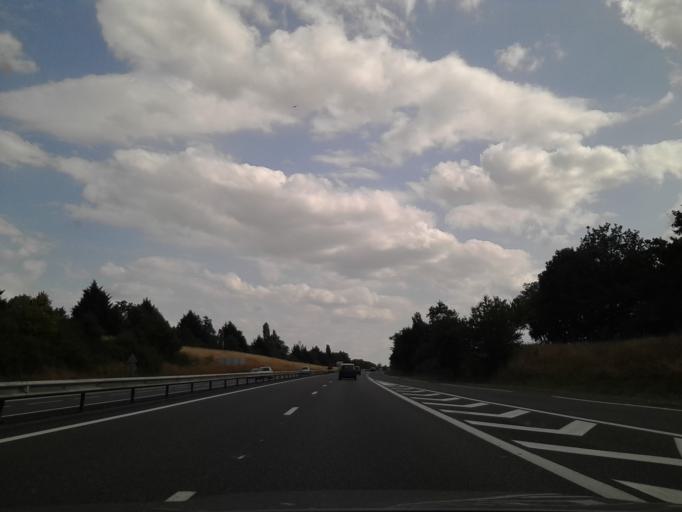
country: FR
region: Auvergne
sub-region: Departement de l'Allier
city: Bellenaves
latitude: 46.2287
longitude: 3.1000
